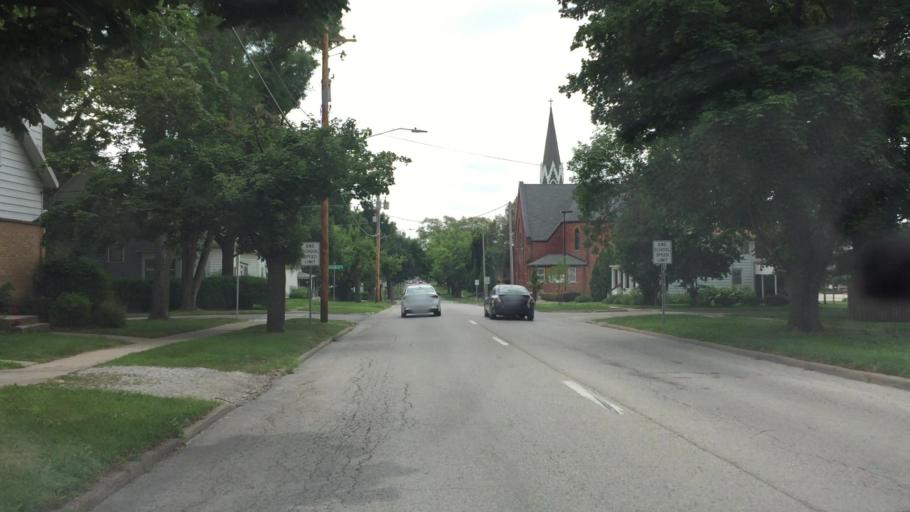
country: US
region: Iowa
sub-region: Johnson County
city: Iowa City
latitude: 41.6672
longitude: -91.5257
